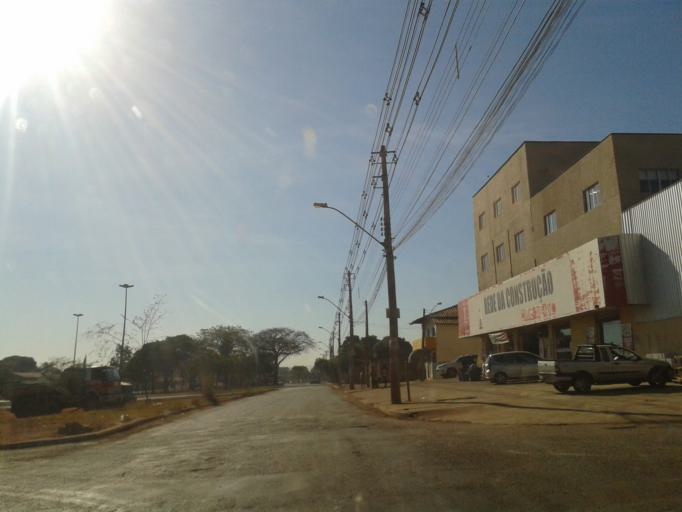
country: BR
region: Goias
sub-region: Goiania
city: Goiania
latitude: -16.6531
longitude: -49.3426
